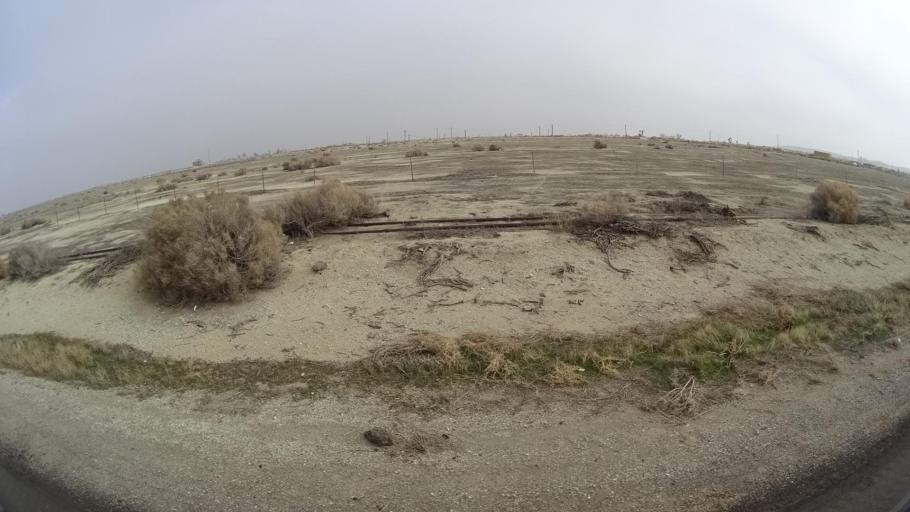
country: US
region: California
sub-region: Kern County
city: Maricopa
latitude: 35.0507
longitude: -119.3671
